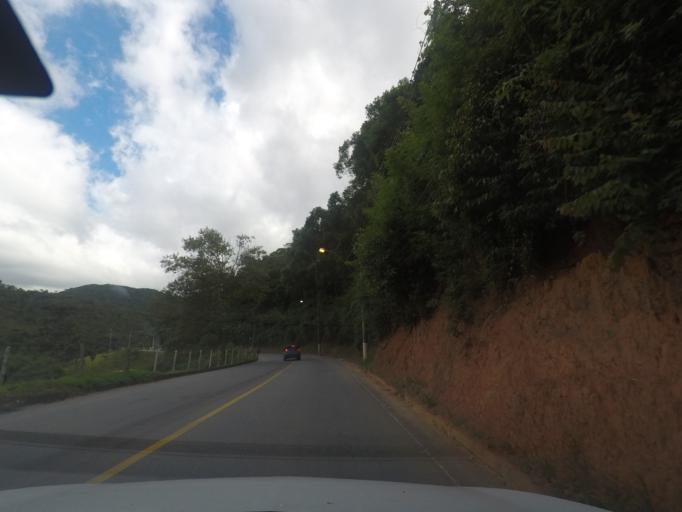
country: BR
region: Rio de Janeiro
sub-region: Teresopolis
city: Teresopolis
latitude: -22.3927
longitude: -42.9567
